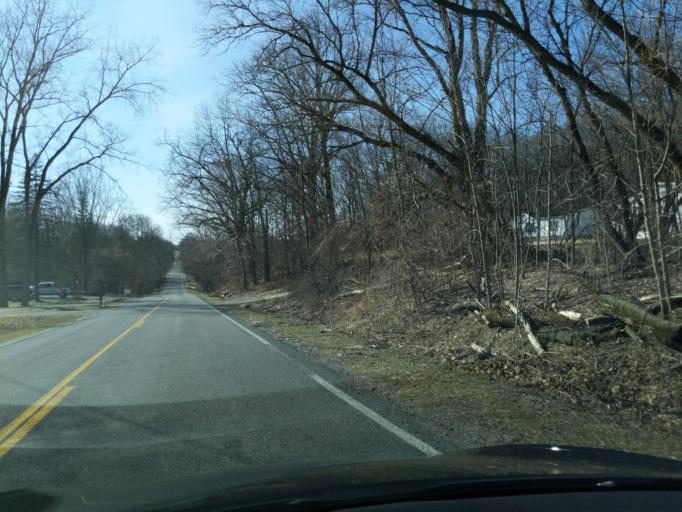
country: US
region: Michigan
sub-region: Ionia County
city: Saranac
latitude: 42.9296
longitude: -85.1778
